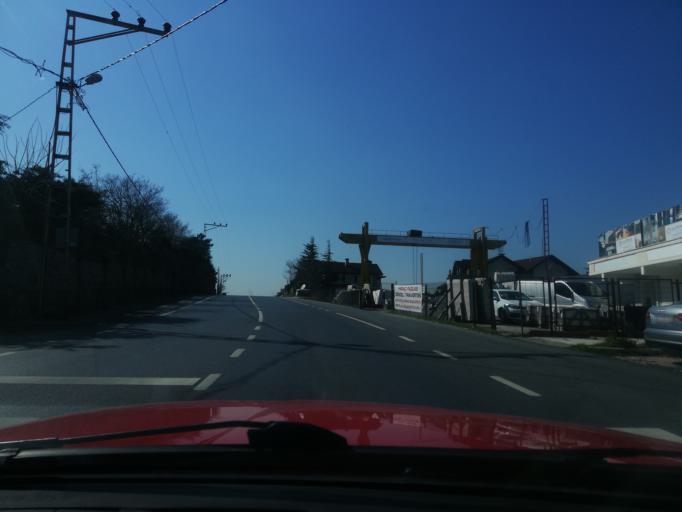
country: TR
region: Istanbul
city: Umraniye
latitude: 41.0733
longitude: 29.1580
